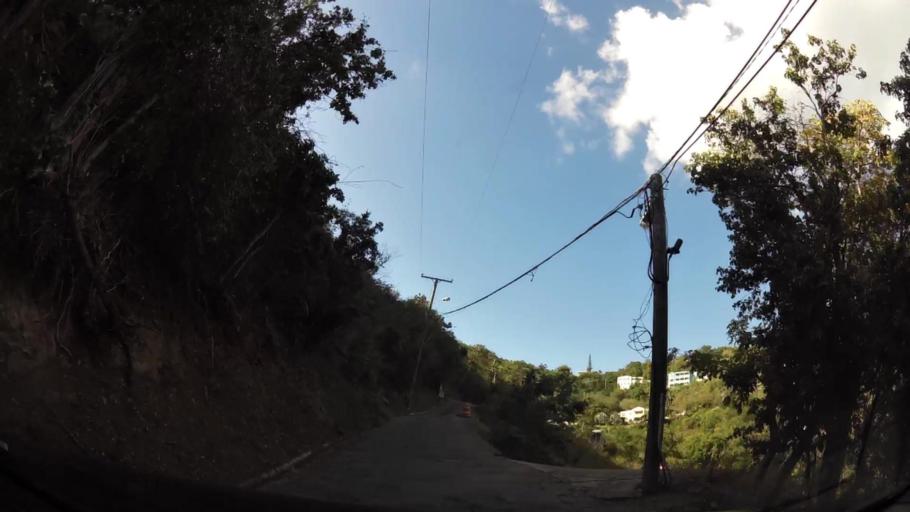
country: VG
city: Road Town
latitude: 18.3924
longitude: -64.6771
